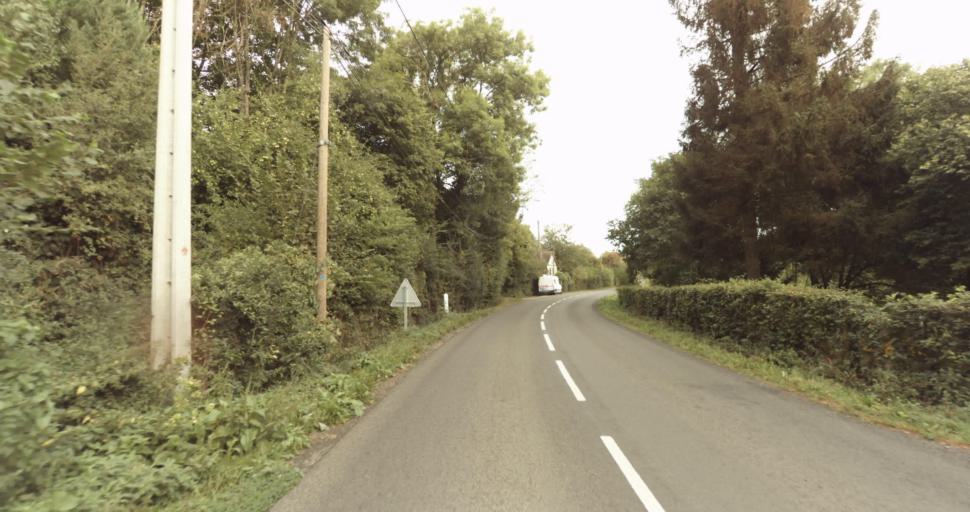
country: FR
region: Lower Normandy
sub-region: Departement de l'Orne
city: Vimoutiers
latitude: 48.9565
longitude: 0.2625
